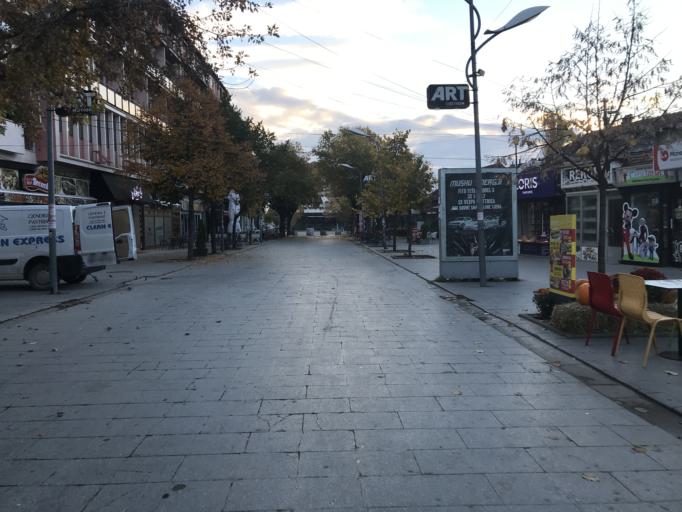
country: XK
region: Pec
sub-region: Komuna e Pejes
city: Peje
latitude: 42.6591
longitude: 20.2871
